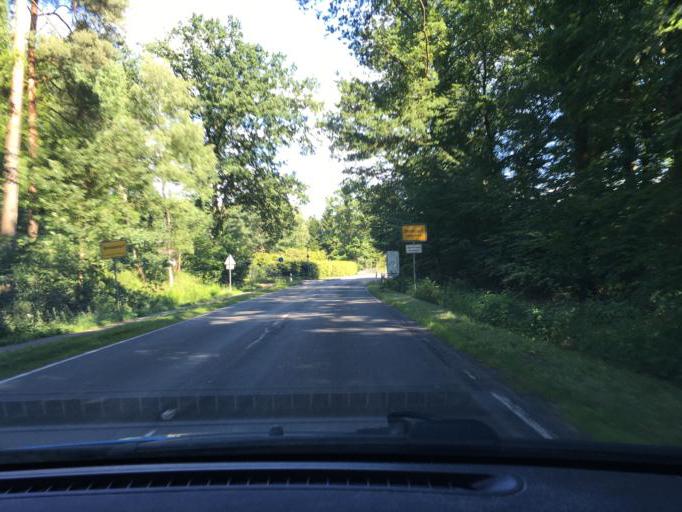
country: DE
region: Lower Saxony
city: Bendestorf
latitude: 53.3427
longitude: 9.9570
